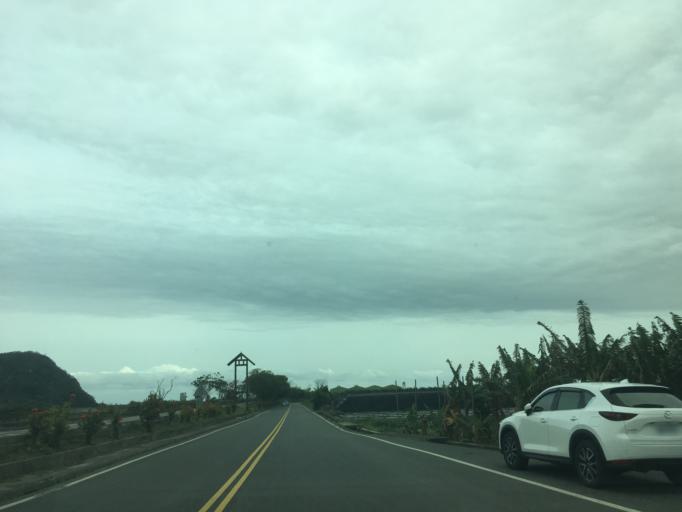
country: TW
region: Taiwan
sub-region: Taitung
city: Taitung
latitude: 22.8053
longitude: 121.1337
